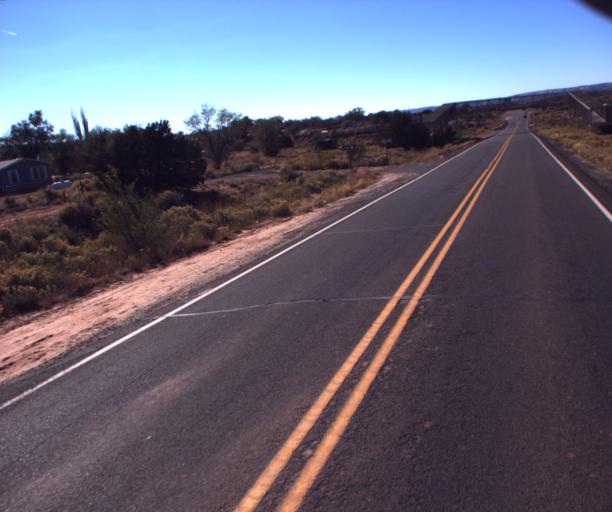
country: US
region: Arizona
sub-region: Apache County
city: Ganado
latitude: 35.7093
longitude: -109.5367
